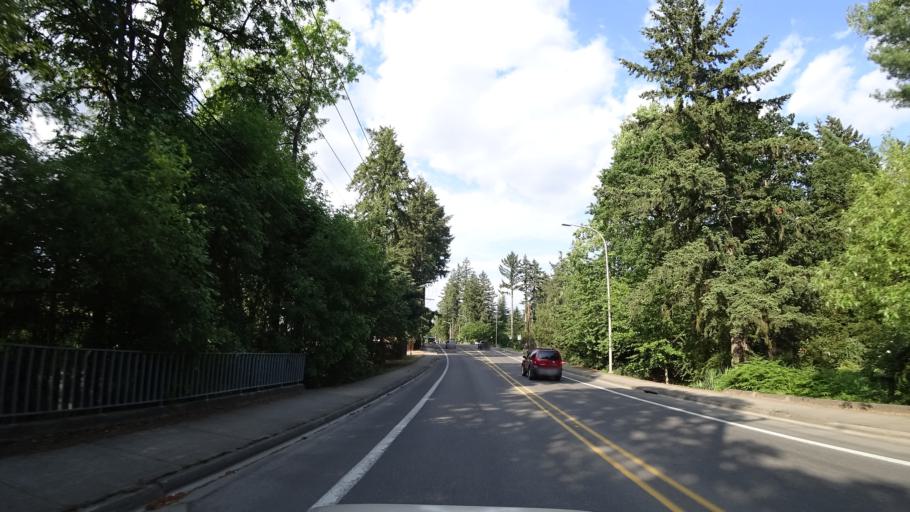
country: US
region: Oregon
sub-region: Washington County
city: Garden Home-Whitford
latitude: 45.4594
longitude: -122.7618
